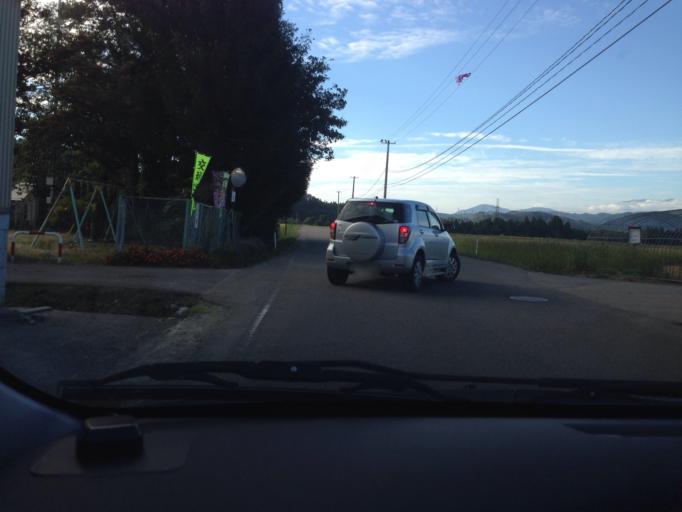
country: JP
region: Fukushima
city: Kitakata
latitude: 37.5903
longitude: 139.7667
